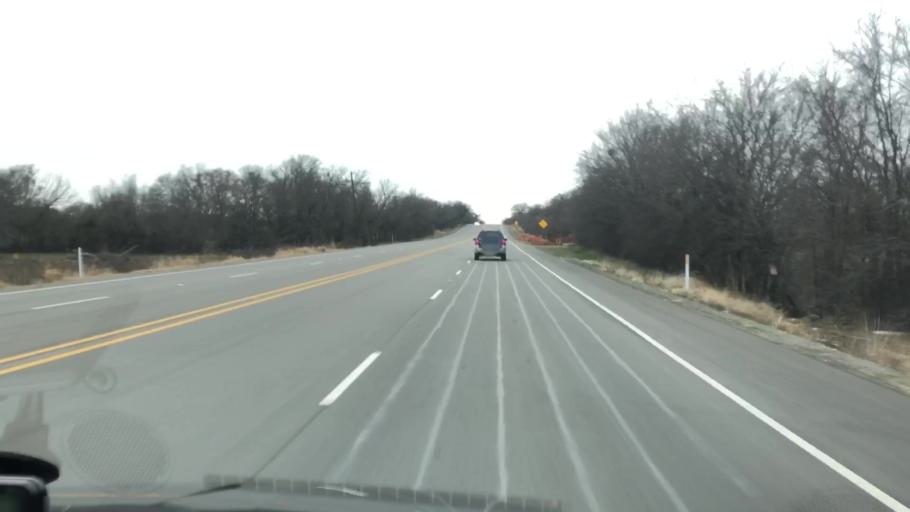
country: US
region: Texas
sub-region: Hamilton County
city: Hico
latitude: 32.0070
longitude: -98.0577
